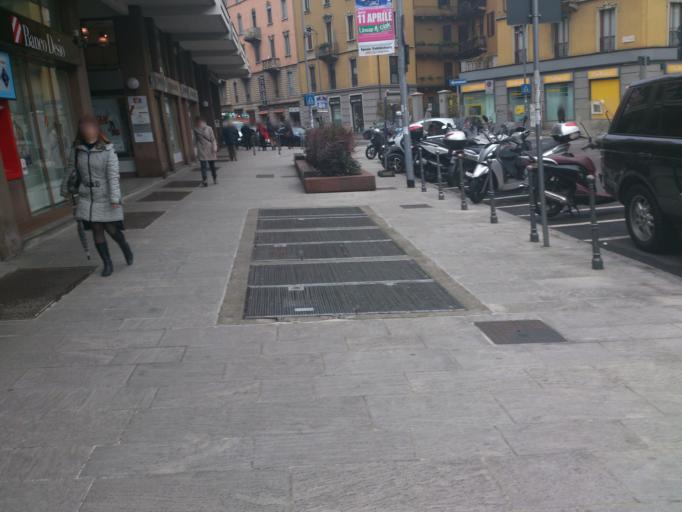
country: IT
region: Lombardy
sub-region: Citta metropolitana di Milano
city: Milano
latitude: 45.4664
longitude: 9.1489
